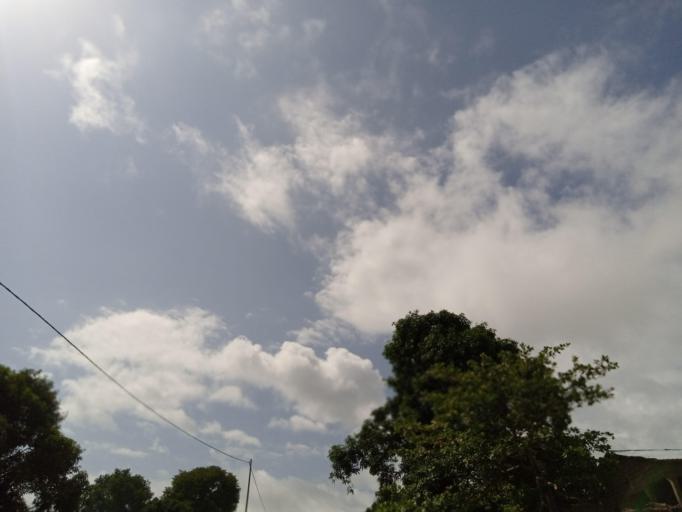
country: SL
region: Northern Province
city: Masoyila
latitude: 8.6063
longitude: -13.2050
